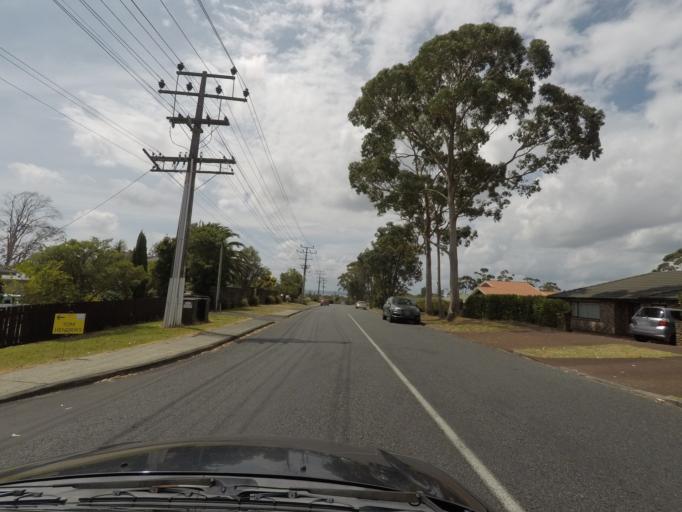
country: NZ
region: Auckland
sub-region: Auckland
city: Waitakere
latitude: -36.8994
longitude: 174.6427
